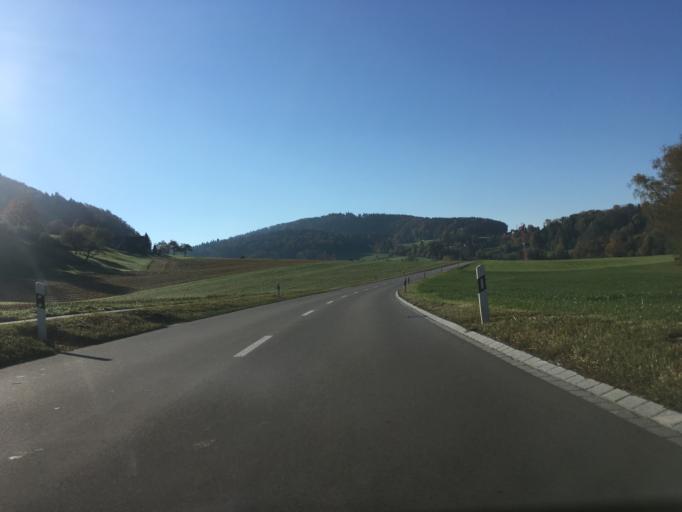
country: CH
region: Zurich
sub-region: Bezirk Affoltern
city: Bonstetten
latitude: 47.2930
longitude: 8.4855
